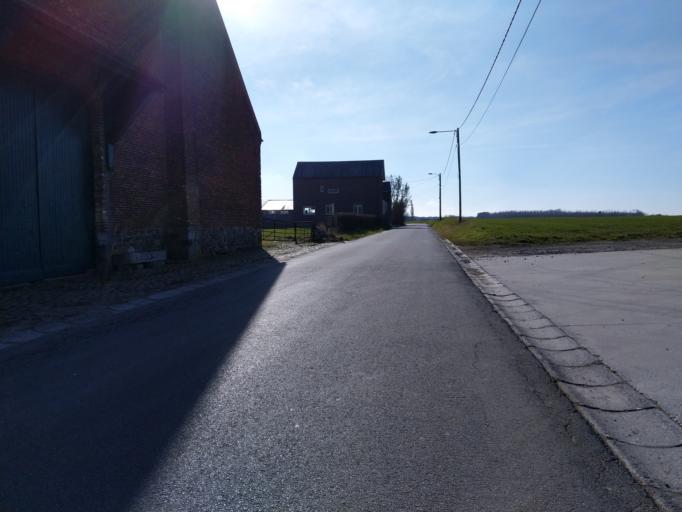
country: FR
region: Nord-Pas-de-Calais
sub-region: Departement du Nord
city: Feignies
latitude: 50.3392
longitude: 3.9008
